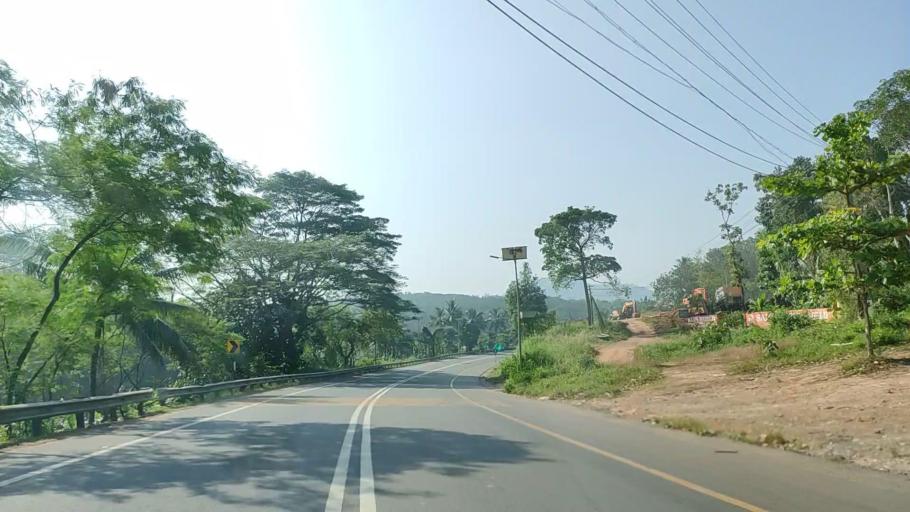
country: IN
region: Kerala
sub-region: Kollam
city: Punalur
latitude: 8.8846
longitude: 76.8693
